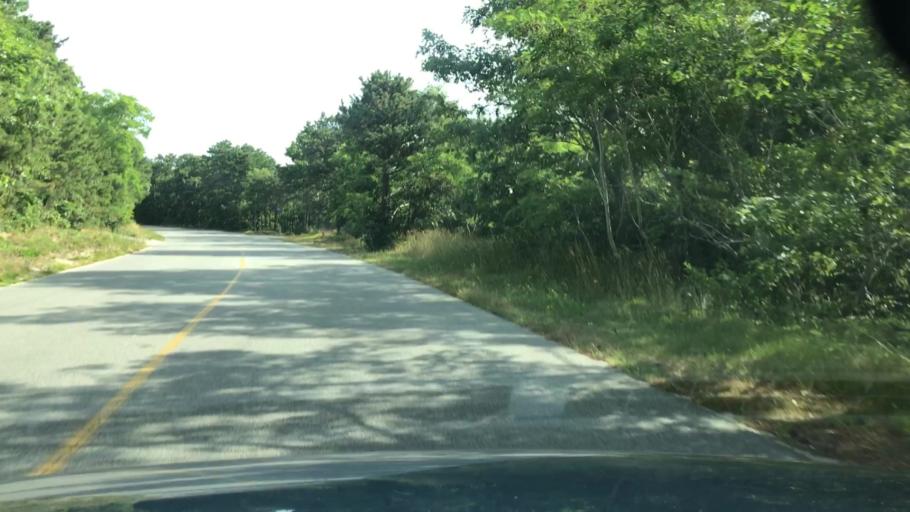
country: US
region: Massachusetts
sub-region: Barnstable County
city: Truro
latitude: 42.0255
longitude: -70.0689
